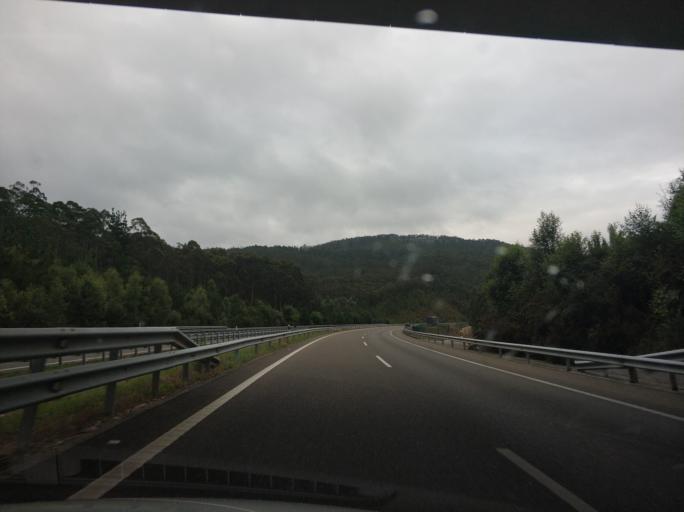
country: ES
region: Galicia
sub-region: Provincia de Lugo
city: Ribadeo
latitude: 43.5329
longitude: -7.0965
